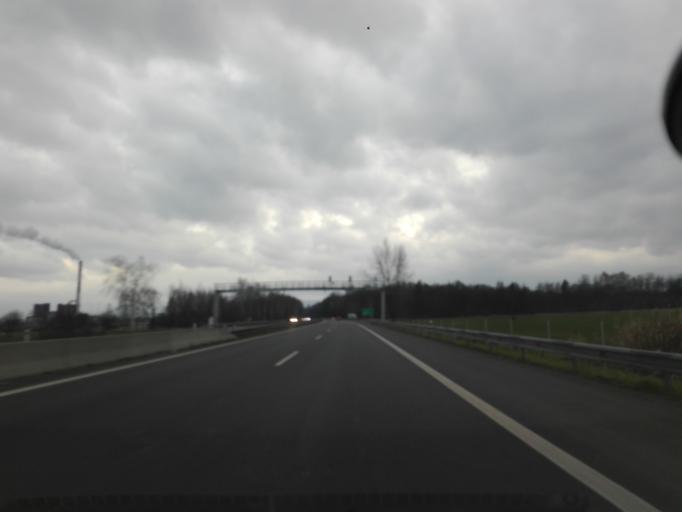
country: CZ
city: Paskov
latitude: 49.7255
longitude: 18.2809
